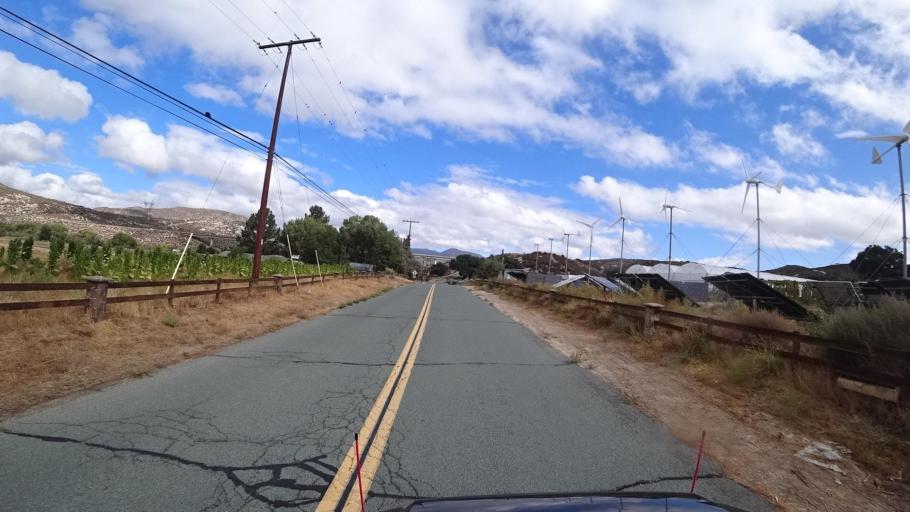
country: US
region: California
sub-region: San Diego County
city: Campo
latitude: 32.7219
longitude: -116.4274
